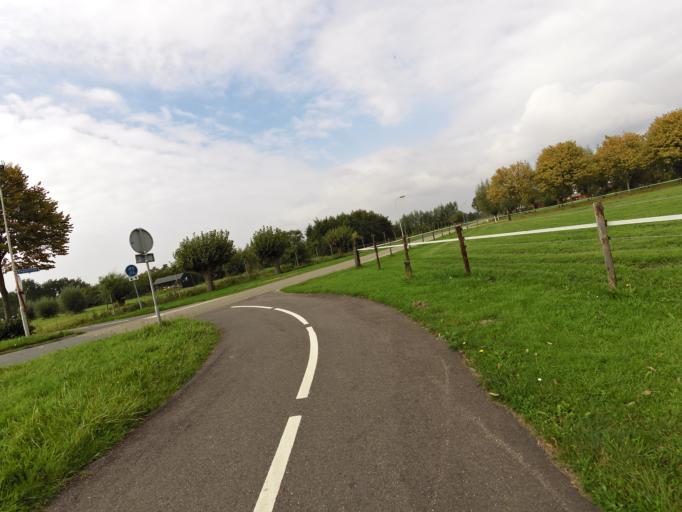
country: NL
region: Gelderland
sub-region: Gemeente Duiven
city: Duiven
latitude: 51.9550
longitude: 6.0085
